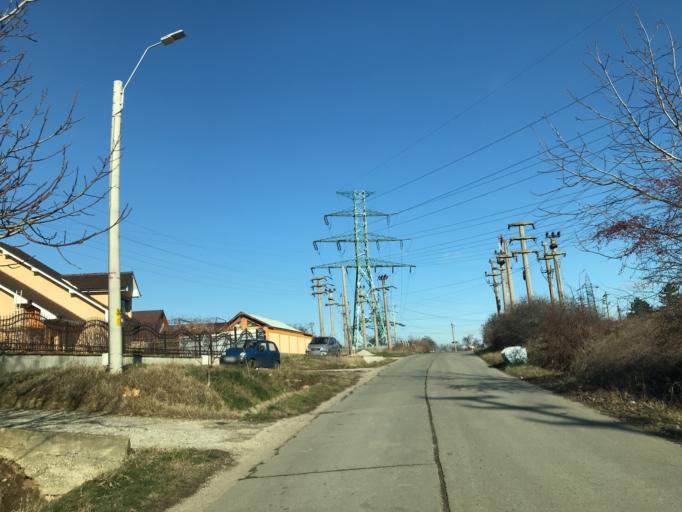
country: RO
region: Olt
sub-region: Municipiul Slatina
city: Slatina
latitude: 44.4144
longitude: 24.3615
